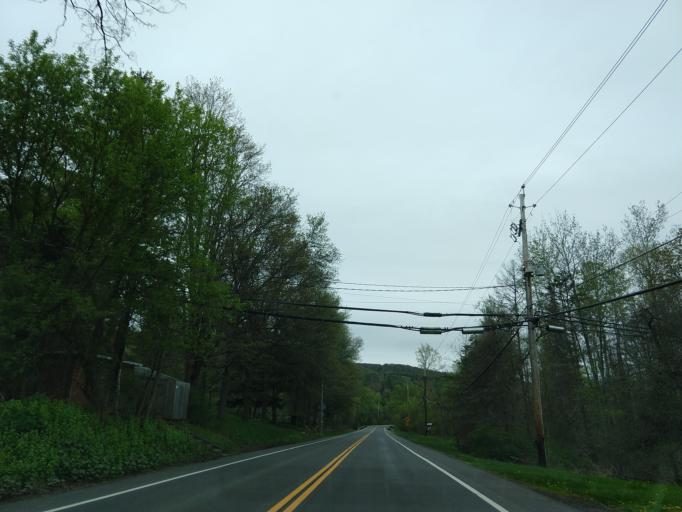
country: US
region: New York
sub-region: Tompkins County
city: Northeast Ithaca
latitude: 42.4844
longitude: -76.3840
